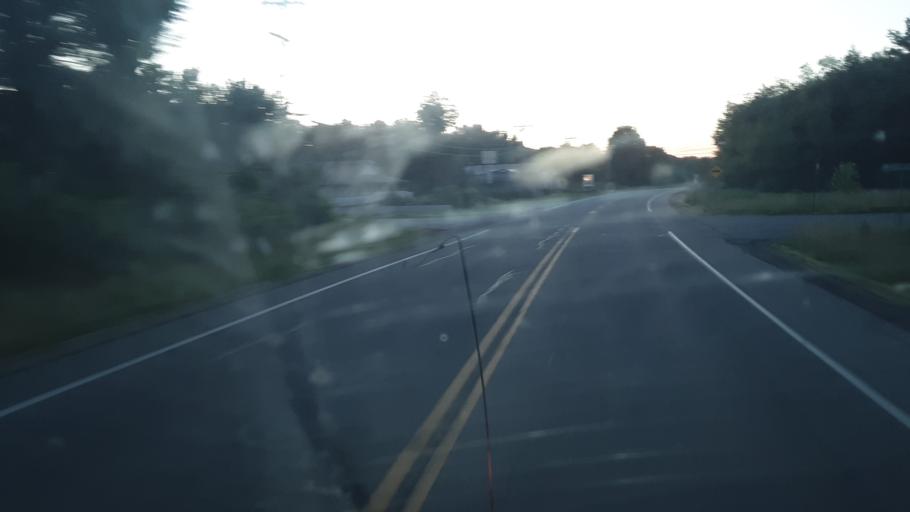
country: US
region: New York
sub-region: Schenectady County
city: East Glenville
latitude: 42.9777
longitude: -73.9556
